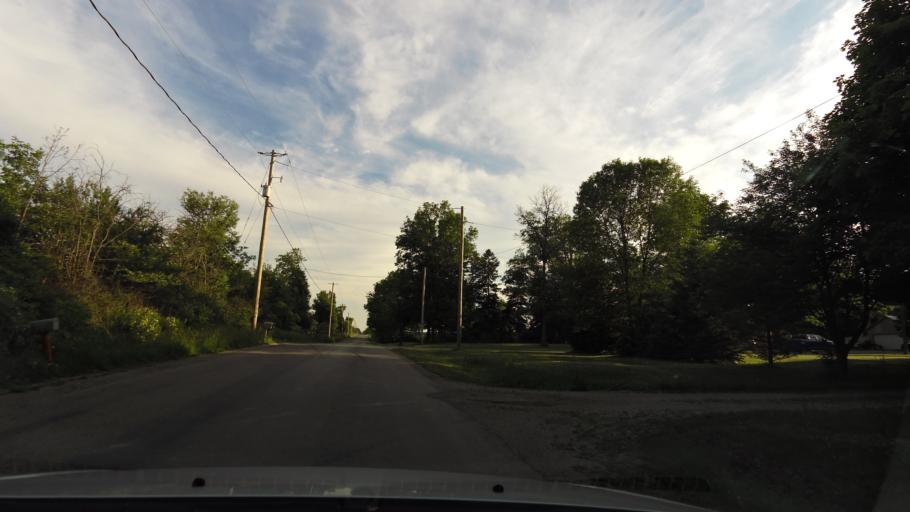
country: CA
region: Ontario
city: Ancaster
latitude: 43.0694
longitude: -79.9831
